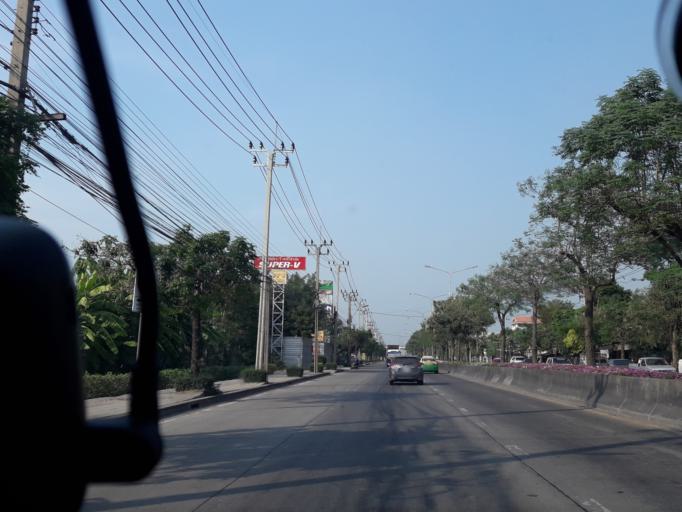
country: TH
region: Bangkok
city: Khlong Sam Wa
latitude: 13.8739
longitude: 100.7317
